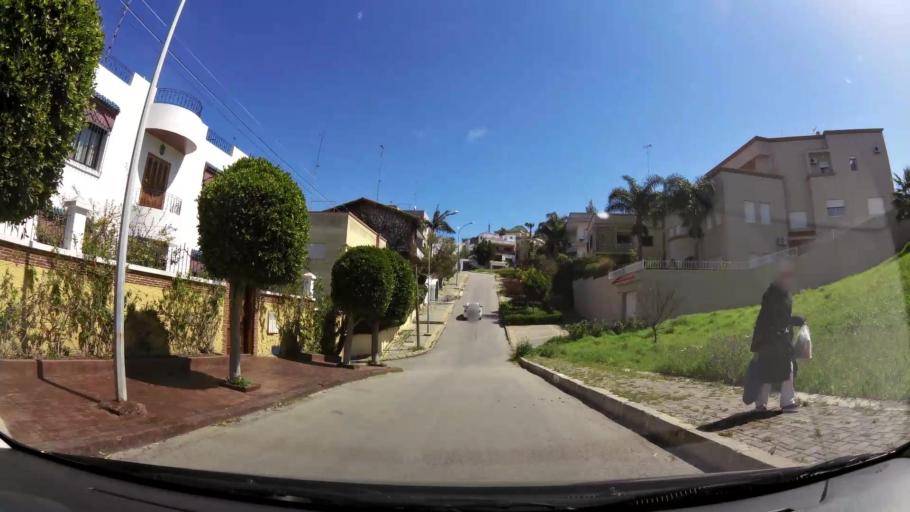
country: MA
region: Tanger-Tetouan
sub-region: Tanger-Assilah
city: Tangier
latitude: 35.7809
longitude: -5.8304
